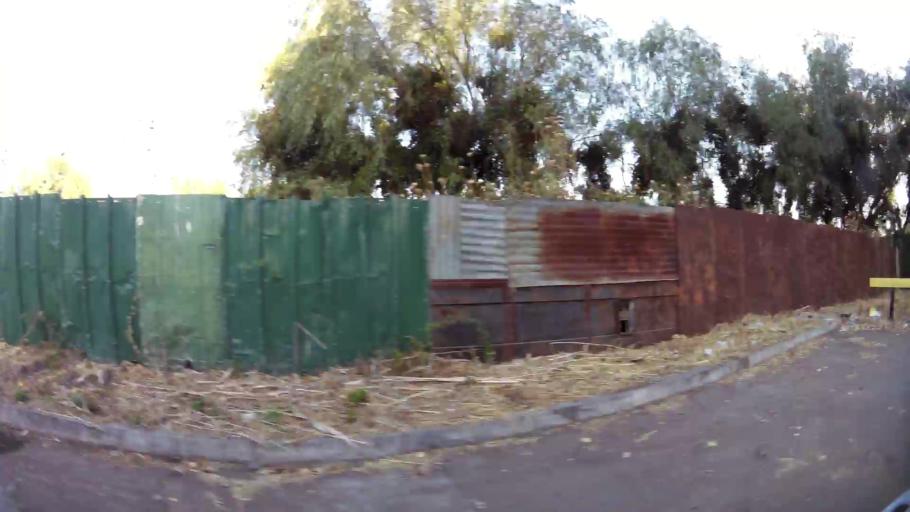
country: CL
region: Maule
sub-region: Provincia de Talca
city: Talca
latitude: -35.4522
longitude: -71.6658
